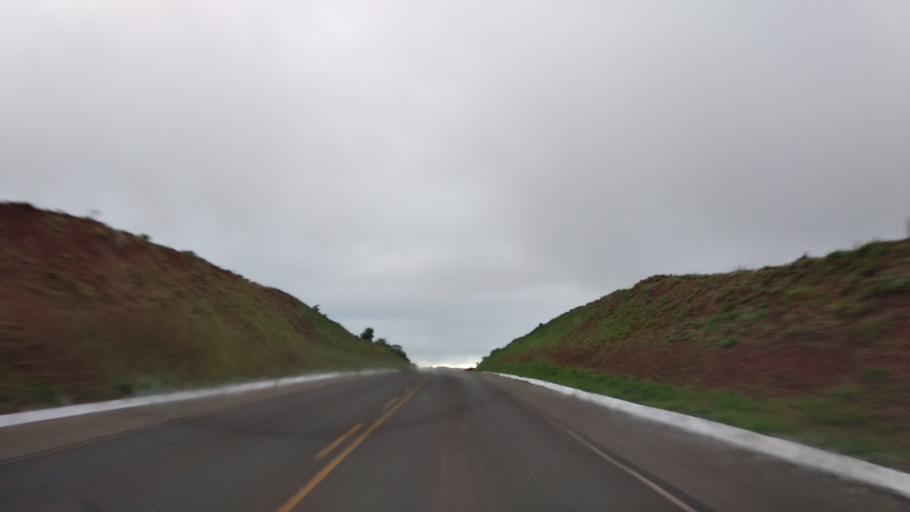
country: BR
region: Santa Catarina
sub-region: Campos Novos
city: Campos Novos
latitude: -27.3859
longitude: -51.0571
